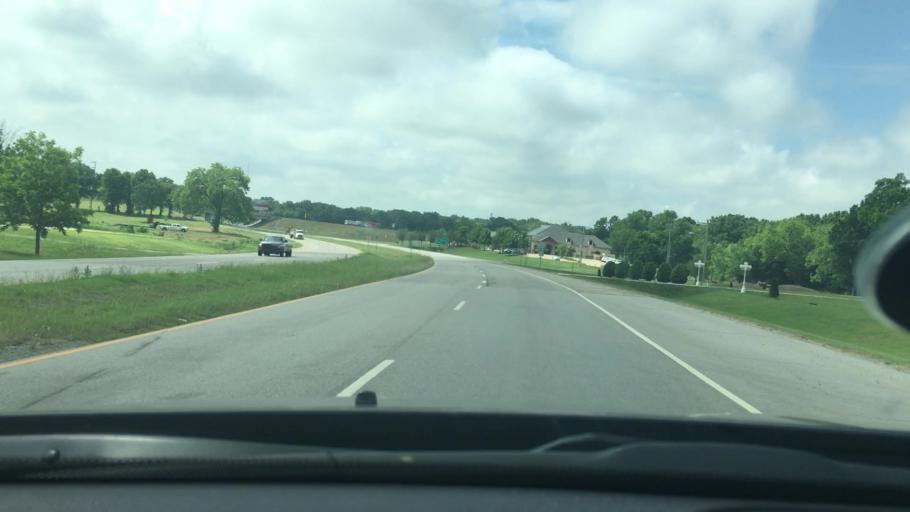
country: US
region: Oklahoma
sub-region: Bryan County
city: Durant
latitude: 34.0425
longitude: -96.3760
